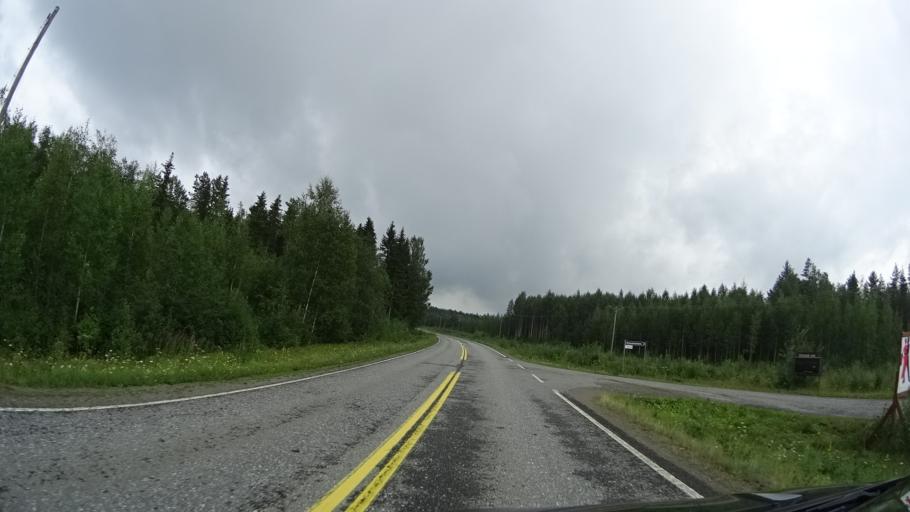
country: FI
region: North Karelia
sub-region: Keski-Karjala
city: Raeaekkylae
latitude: 62.3115
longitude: 29.5188
